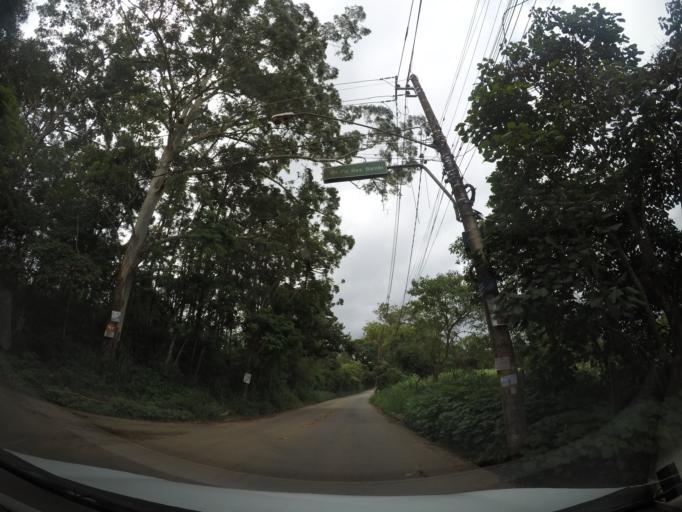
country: BR
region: Sao Paulo
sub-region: Aruja
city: Aruja
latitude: -23.3858
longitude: -46.3969
